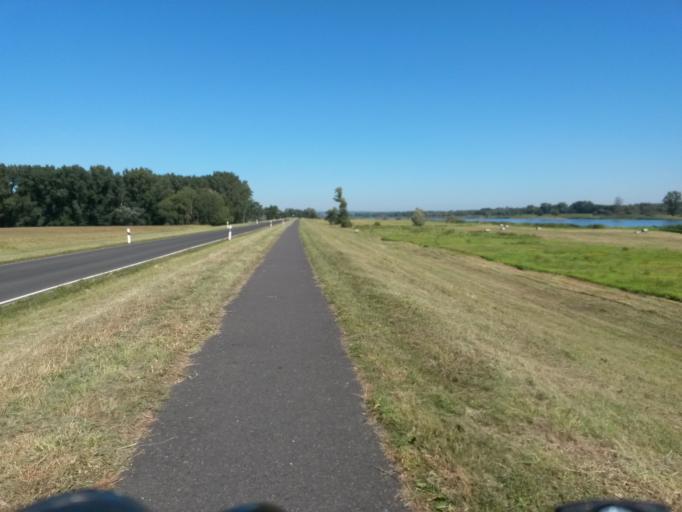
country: PL
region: West Pomeranian Voivodeship
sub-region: Powiat gryfinski
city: Cedynia
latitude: 52.8572
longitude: 14.1308
